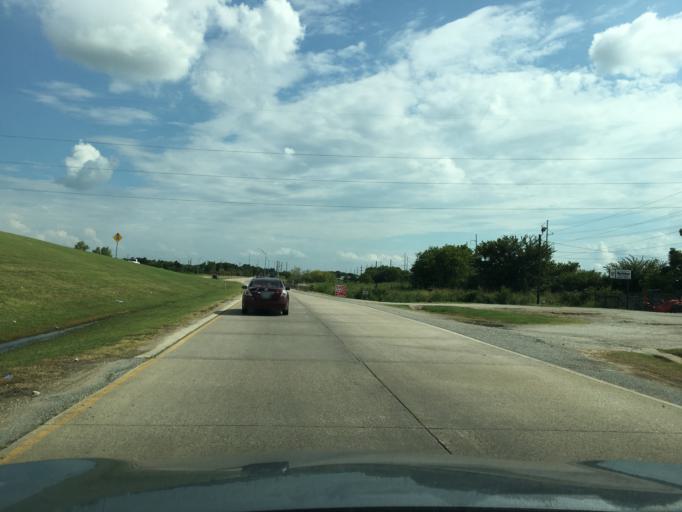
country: US
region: Texas
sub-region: Denton County
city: Denton
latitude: 33.2324
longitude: -97.0904
